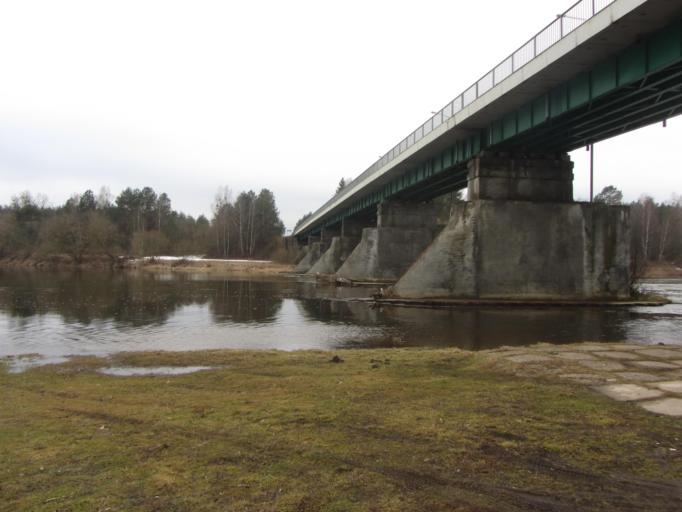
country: LT
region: Alytaus apskritis
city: Druskininkai
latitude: 54.1577
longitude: 24.1812
